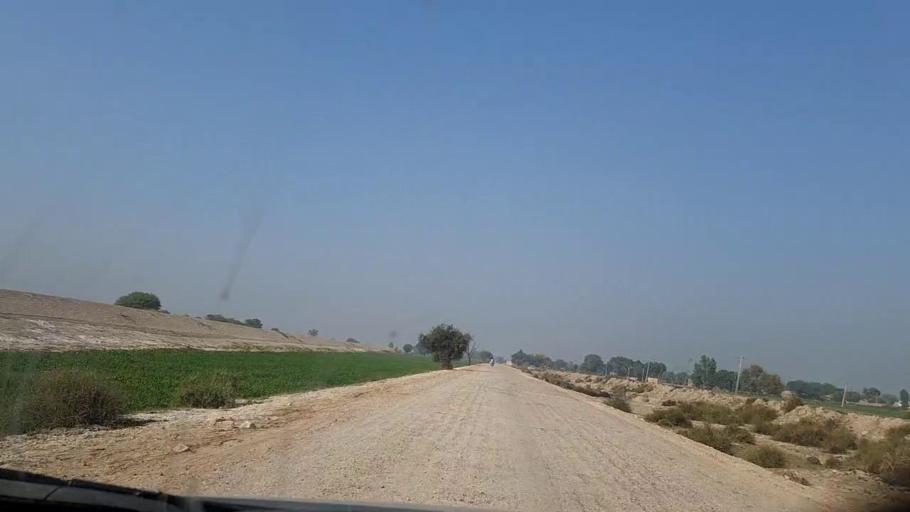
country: PK
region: Sindh
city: Moro
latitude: 26.7273
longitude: 67.9214
